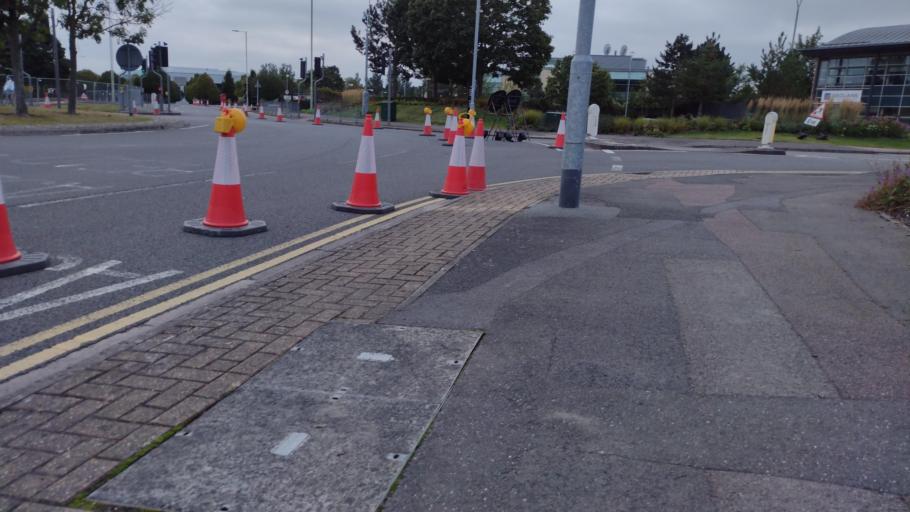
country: GB
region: England
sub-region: Wokingham
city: Winnersh
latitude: 51.4369
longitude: -0.8894
